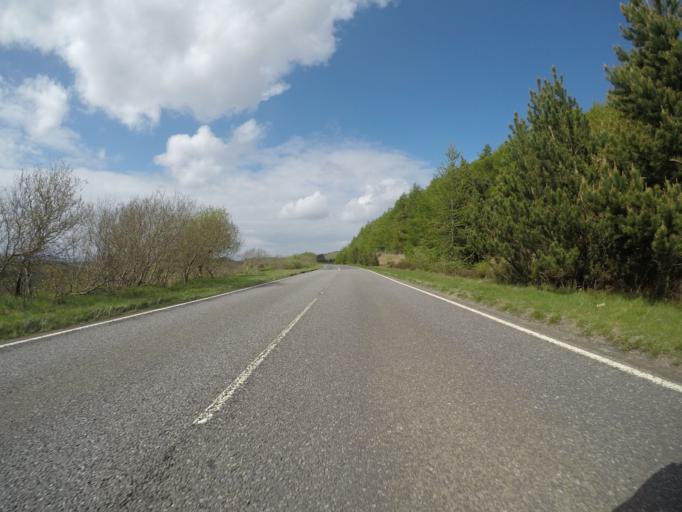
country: GB
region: Scotland
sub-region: Highland
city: Portree
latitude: 57.5254
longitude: -6.3453
